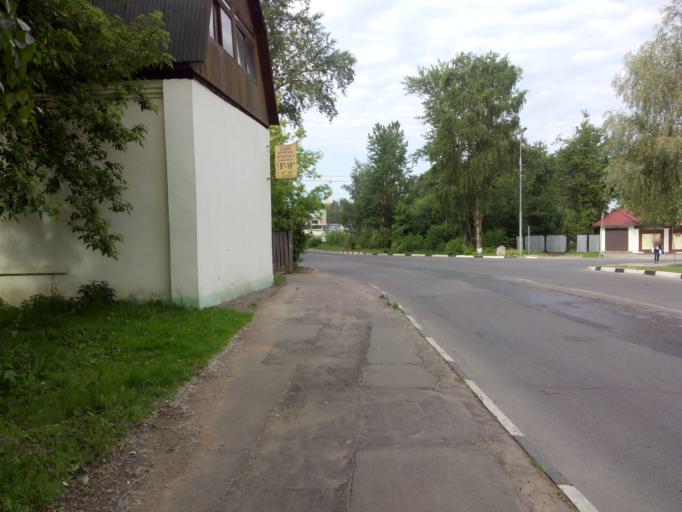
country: RU
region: Moskovskaya
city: Odintsovo
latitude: 55.6613
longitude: 37.2876
